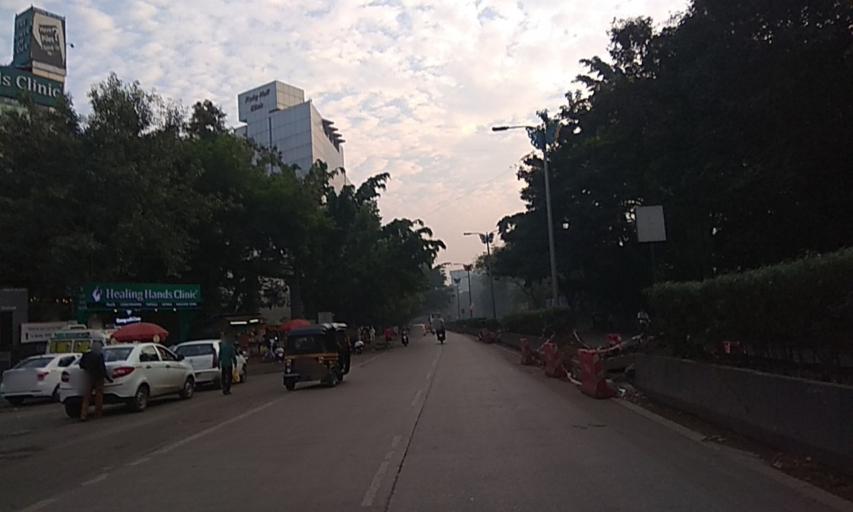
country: IN
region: Maharashtra
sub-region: Pune Division
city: Shivaji Nagar
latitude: 18.5319
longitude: 73.8768
